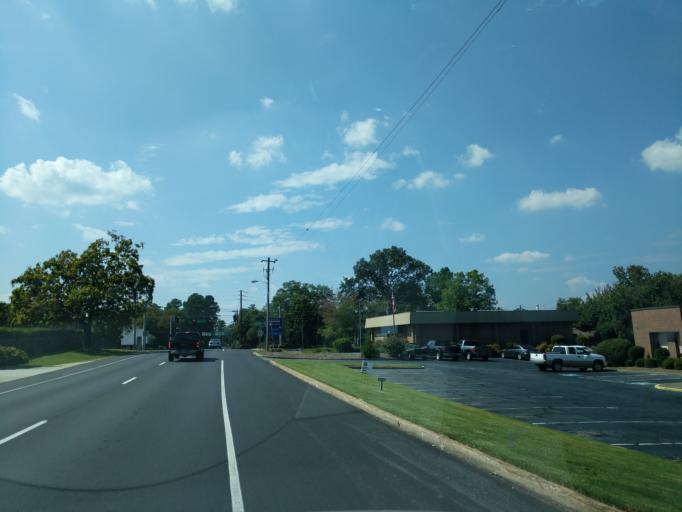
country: US
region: Georgia
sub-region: Hart County
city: Hartwell
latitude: 34.3541
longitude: -82.9352
